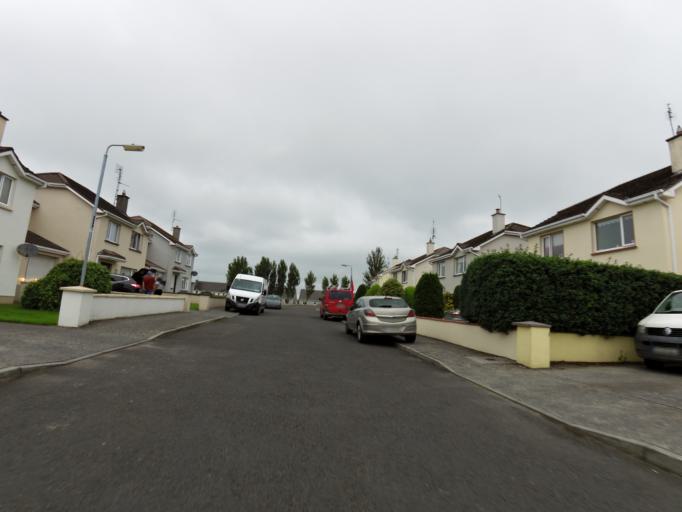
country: IE
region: Connaught
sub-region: County Galway
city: Loughrea
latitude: 53.2023
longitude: -8.5556
